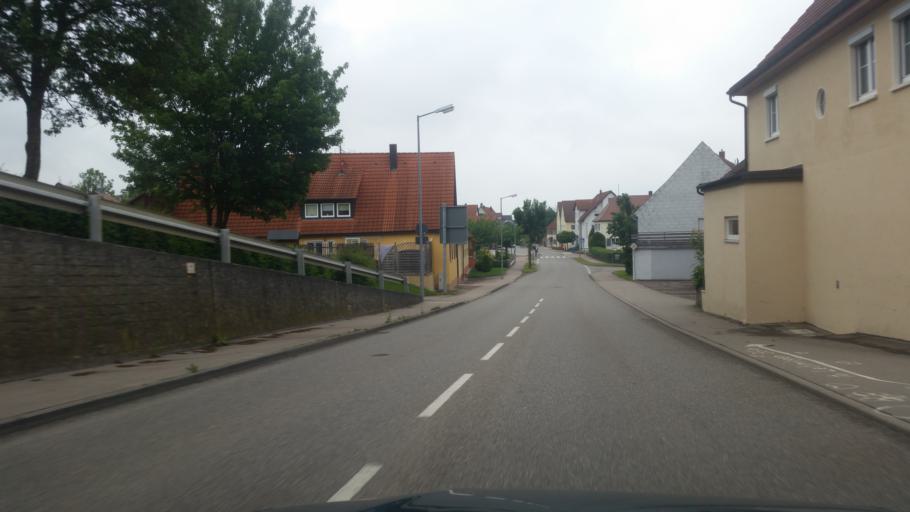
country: DE
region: Baden-Wuerttemberg
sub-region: Regierungsbezirk Stuttgart
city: Westhausen
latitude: 48.9408
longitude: 10.2128
